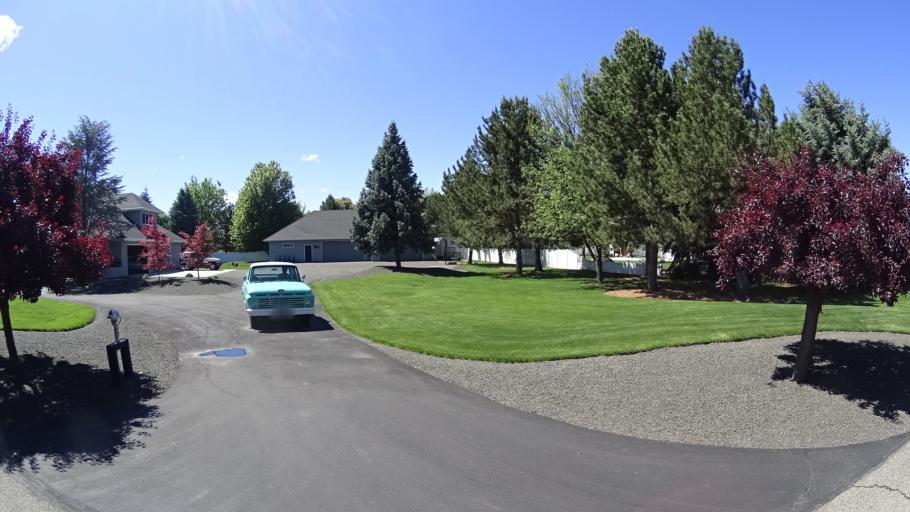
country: US
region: Idaho
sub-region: Ada County
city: Eagle
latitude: 43.6690
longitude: -116.3889
